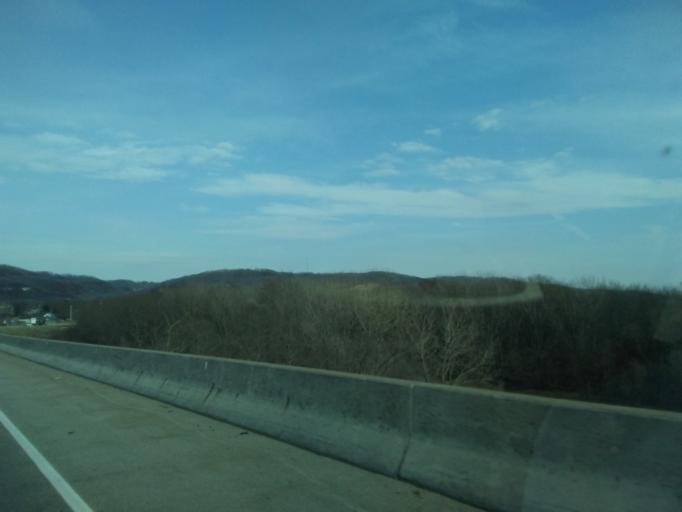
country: US
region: Wisconsin
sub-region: Crawford County
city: Prairie du Chien
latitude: 43.0477
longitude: -91.1567
